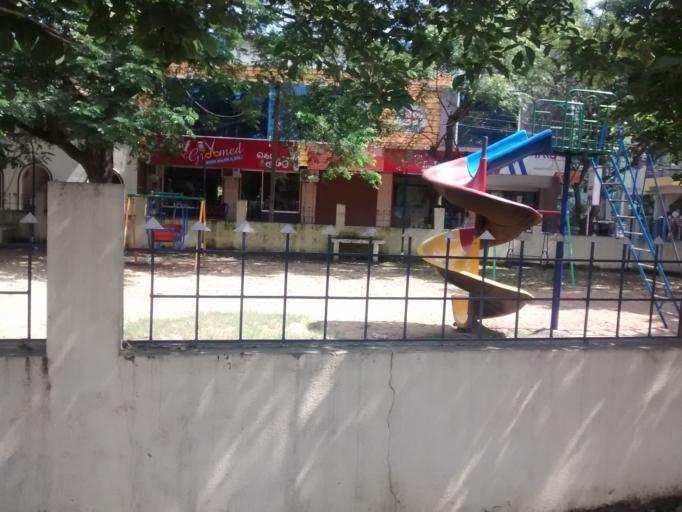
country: IN
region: Tamil Nadu
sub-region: Kancheepuram
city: Pallavaram
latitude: 12.9392
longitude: 80.1383
